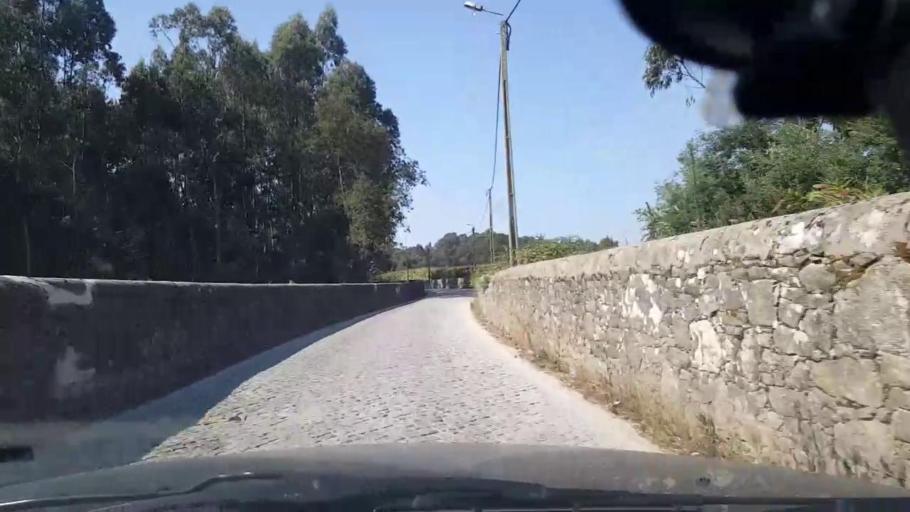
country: PT
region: Porto
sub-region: Povoa de Varzim
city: Pedroso
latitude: 41.3894
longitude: -8.7098
